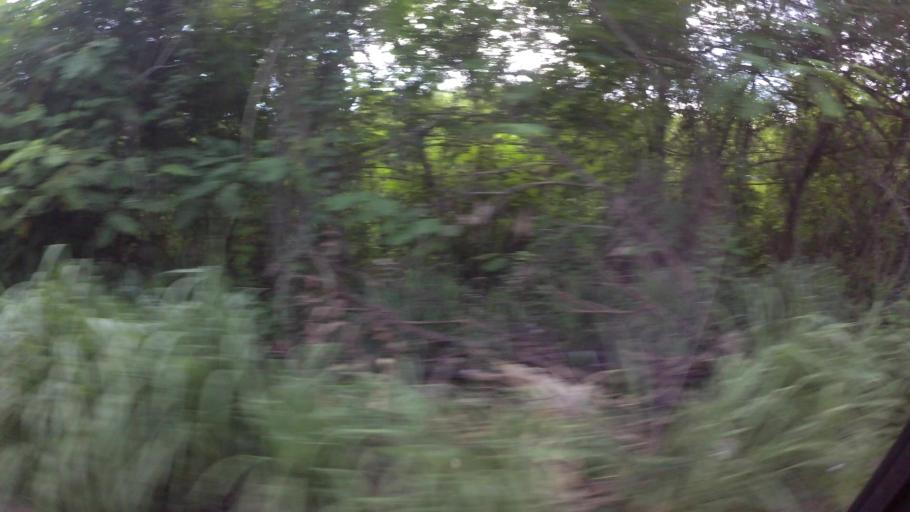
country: TH
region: Chon Buri
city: Sattahip
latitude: 12.6872
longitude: 100.9260
